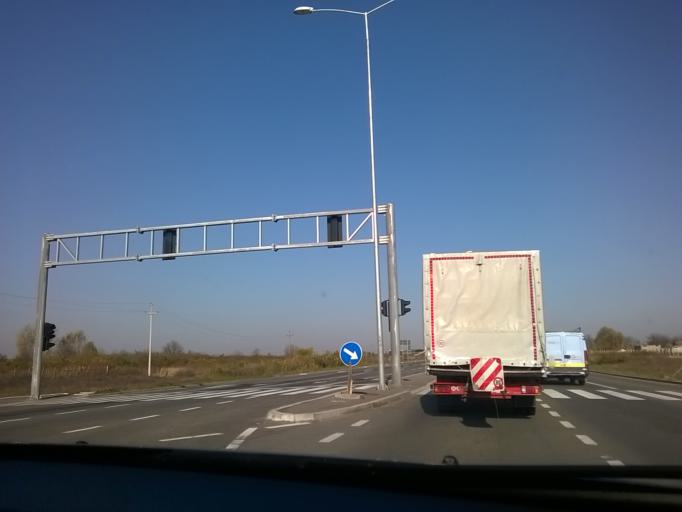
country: RS
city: Ovca
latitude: 44.8505
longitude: 20.5174
